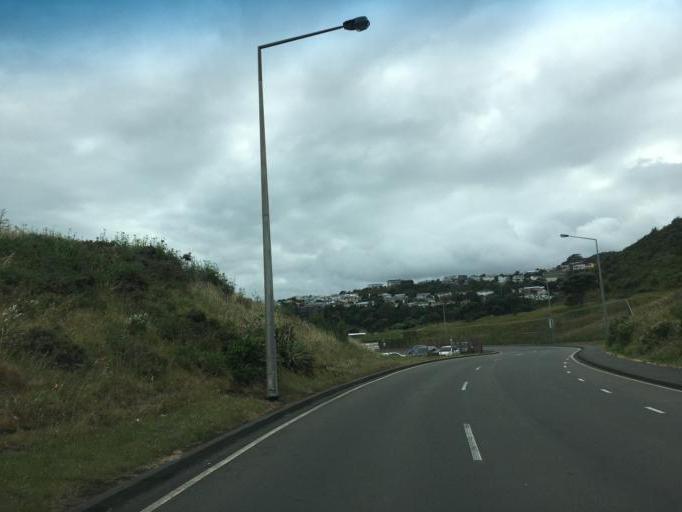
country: NZ
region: Wellington
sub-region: Wellington City
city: Wellington
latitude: -41.3344
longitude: 174.8109
